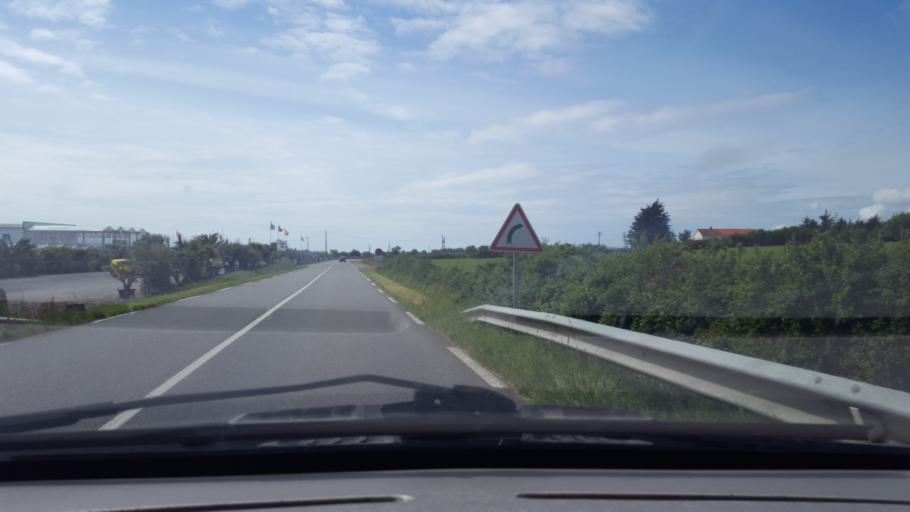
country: FR
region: Pays de la Loire
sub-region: Departement de la Loire-Atlantique
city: Bourgneuf-en-Retz
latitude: 47.0324
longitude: -1.9234
